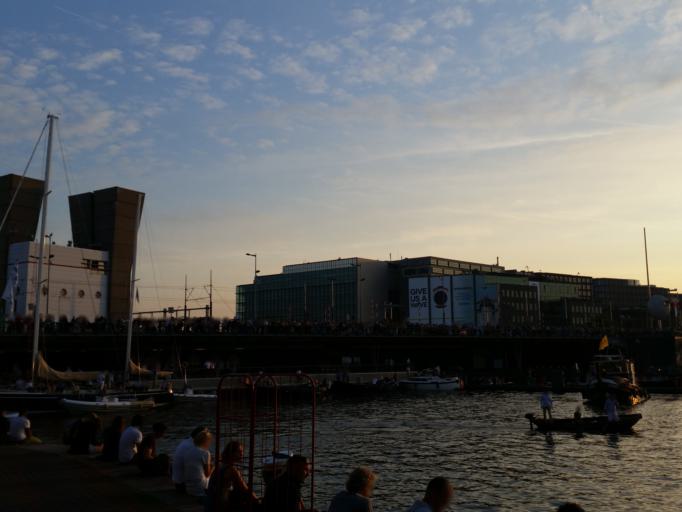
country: NL
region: North Holland
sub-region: Gemeente Amsterdam
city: Amsterdam
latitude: 52.3782
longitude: 4.9124
